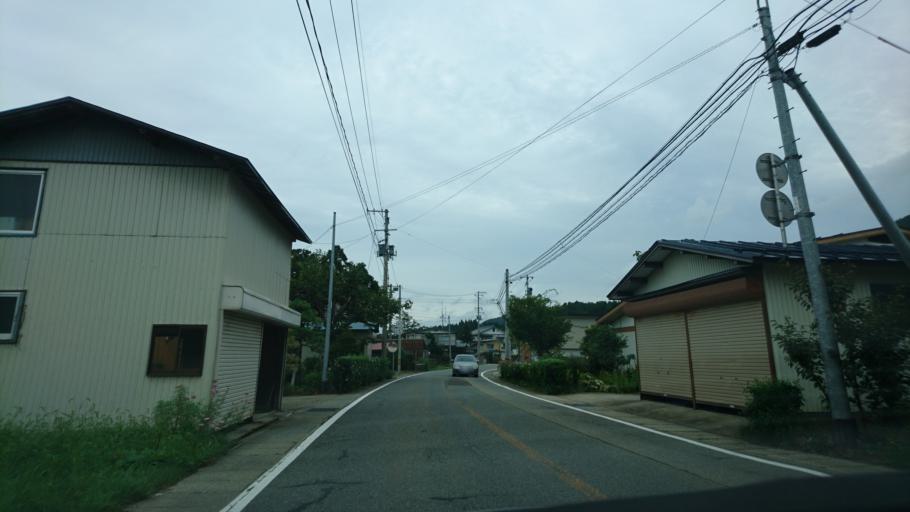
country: JP
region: Akita
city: Yuzawa
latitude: 39.1361
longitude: 140.5753
